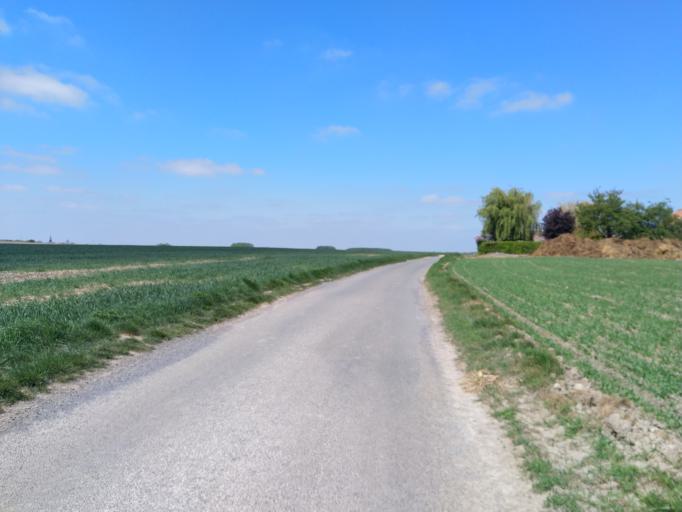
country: BE
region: Wallonia
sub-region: Province du Hainaut
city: Chievres
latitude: 50.5251
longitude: 3.8153
